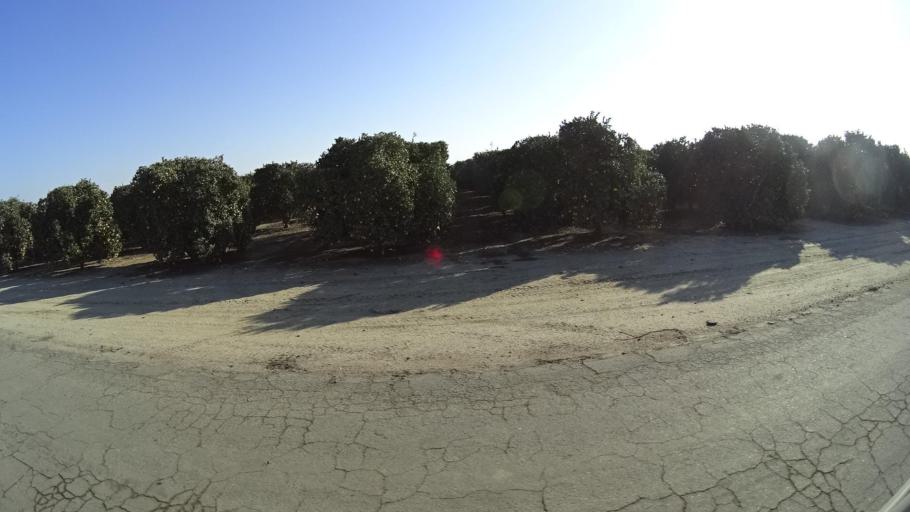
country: US
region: California
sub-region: Tulare County
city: Richgrove
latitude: 35.7742
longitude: -119.1518
